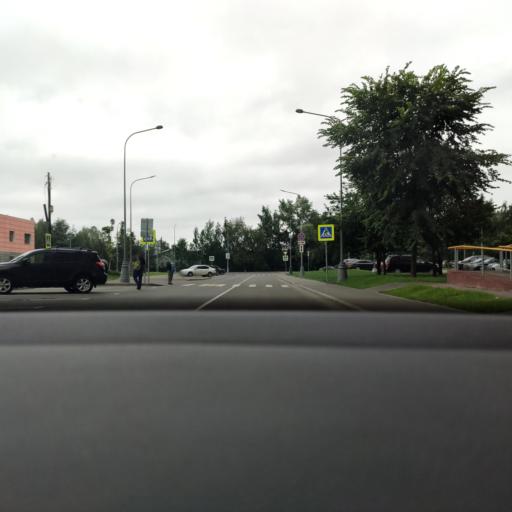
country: RU
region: Moscow
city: Severnyy
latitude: 55.9332
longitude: 37.5555
